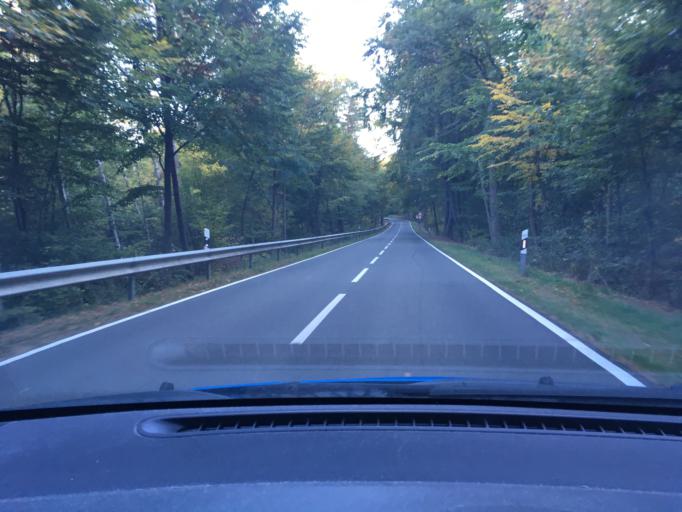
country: DE
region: Lower Saxony
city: Tosterglope
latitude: 53.2530
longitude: 10.8216
